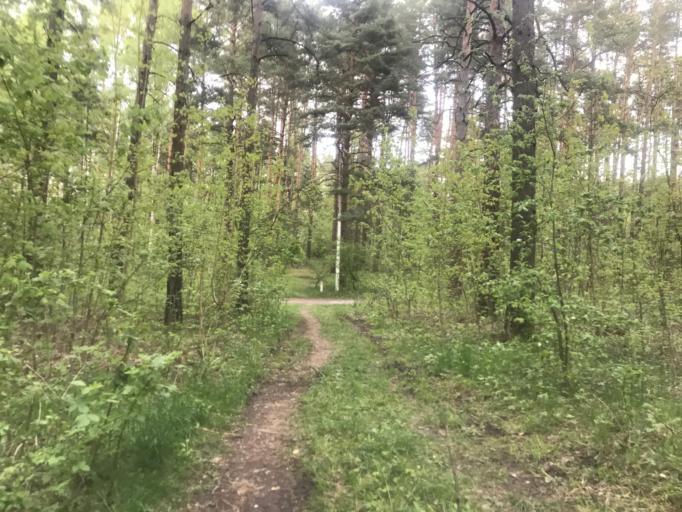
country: BY
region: Minsk
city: Zhdanovichy
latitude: 53.9537
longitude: 27.4239
